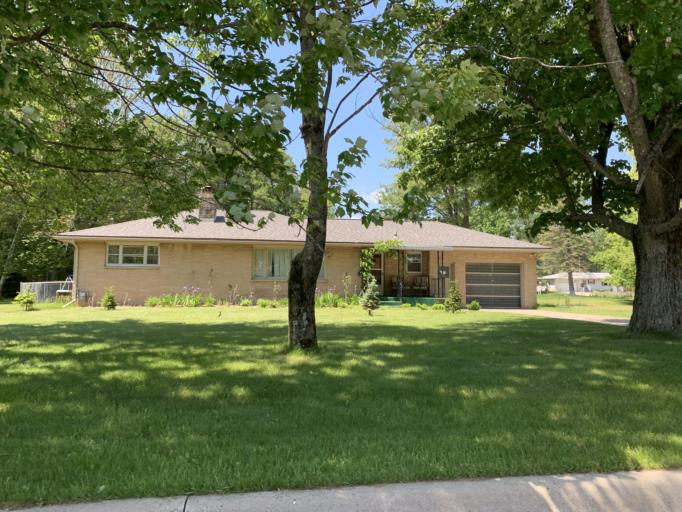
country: US
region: Michigan
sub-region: Menominee County
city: Menominee
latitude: 45.1420
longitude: -87.6173
